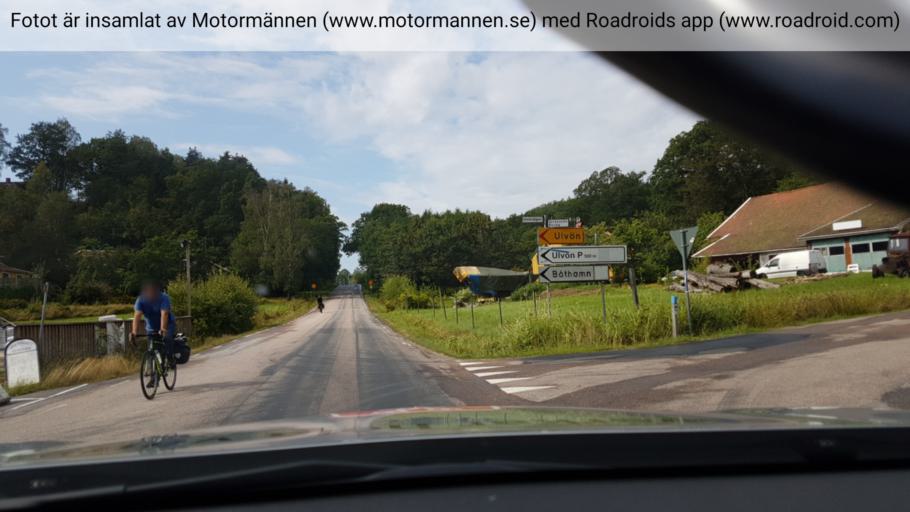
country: SE
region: Vaestra Goetaland
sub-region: Uddevalla Kommun
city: Ljungskile
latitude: 58.2245
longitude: 11.8889
